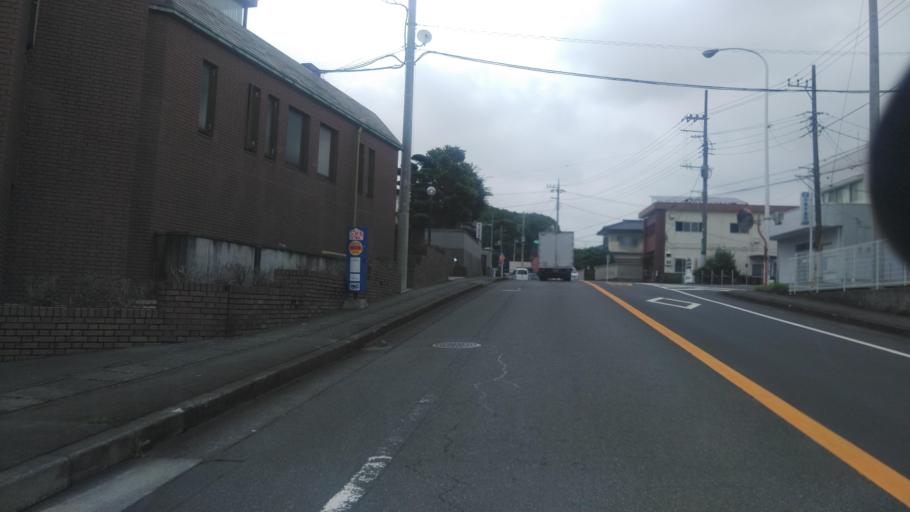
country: JP
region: Shizuoka
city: Fujinomiya
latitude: 35.2277
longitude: 138.6155
